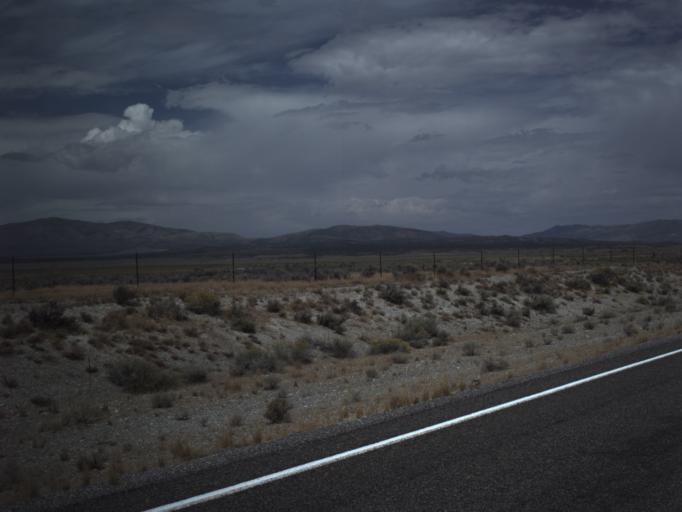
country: US
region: Idaho
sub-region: Cassia County
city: Burley
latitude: 41.6576
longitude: -113.5489
